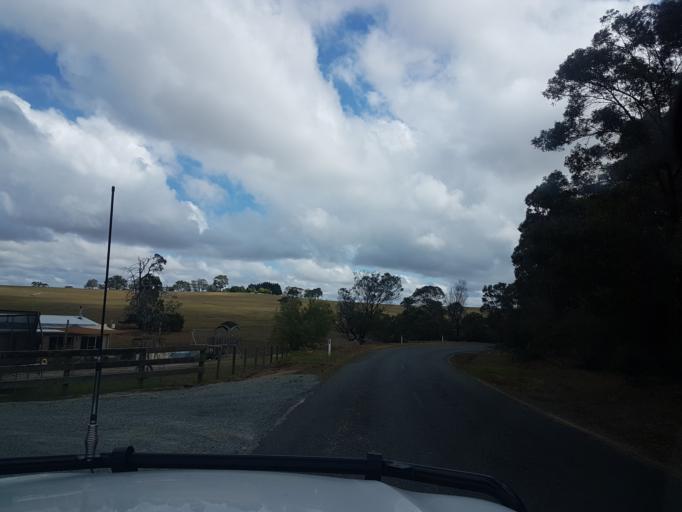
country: AU
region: Victoria
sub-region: East Gippsland
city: Bairnsdale
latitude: -37.7894
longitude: 147.5845
